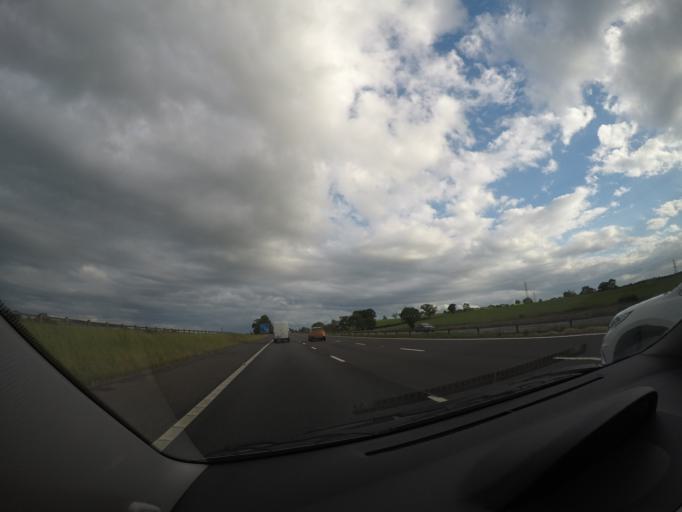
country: GB
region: England
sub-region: Cumbria
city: Penrith
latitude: 54.7065
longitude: -2.7924
